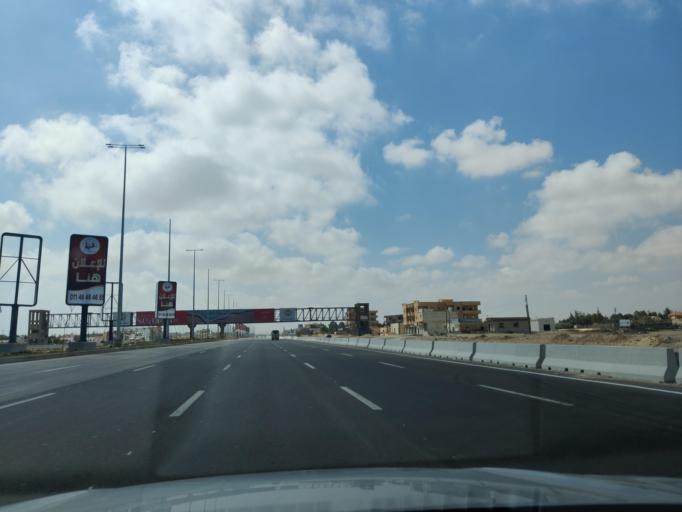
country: EG
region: Muhafazat Matruh
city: Al `Alamayn
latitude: 30.9487
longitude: 28.7741
